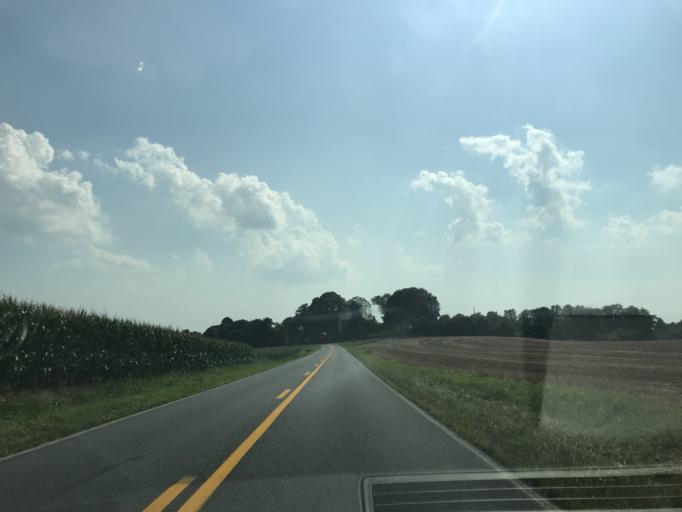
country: US
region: Maryland
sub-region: Carroll County
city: Westminster
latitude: 39.6274
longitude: -76.9688
